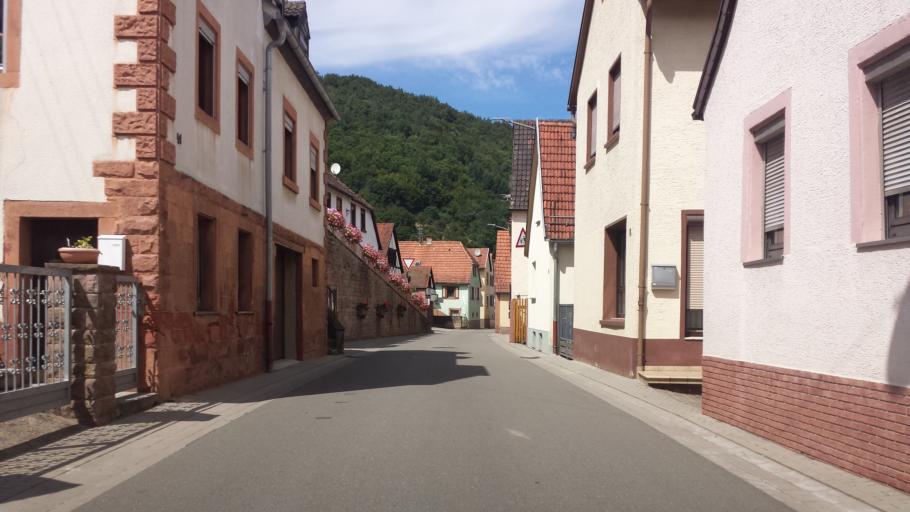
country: DE
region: Rheinland-Pfalz
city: Dernbach
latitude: 49.2475
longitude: 8.0059
